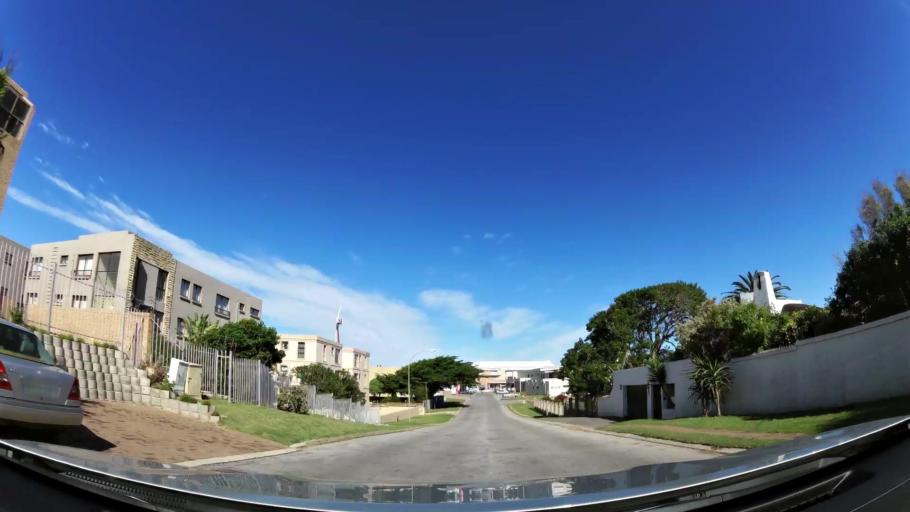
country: ZA
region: Eastern Cape
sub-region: Cacadu District Municipality
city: Jeffrey's Bay
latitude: -34.0506
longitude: 24.9243
